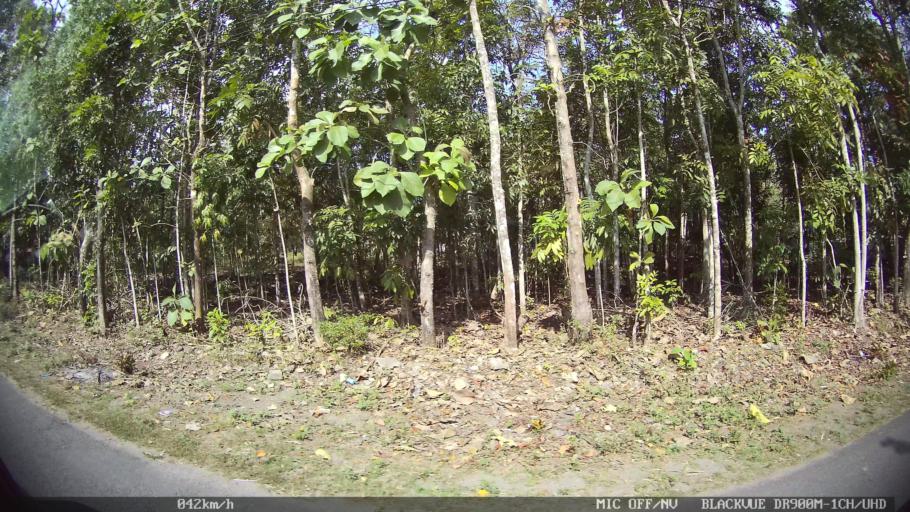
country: ID
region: Daerah Istimewa Yogyakarta
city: Kasihan
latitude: -7.8555
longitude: 110.3014
